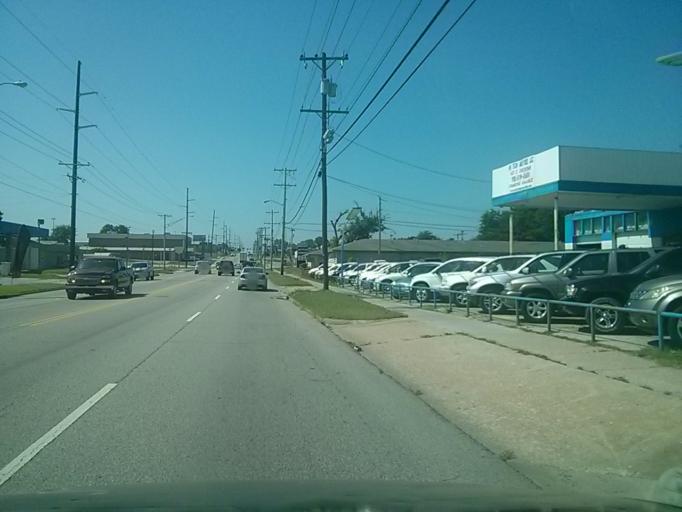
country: US
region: Oklahoma
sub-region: Tulsa County
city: Tulsa
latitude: 36.1526
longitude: -95.9046
